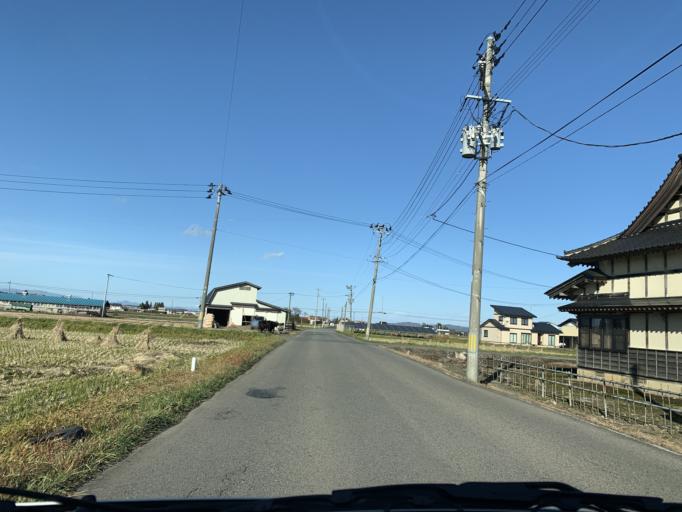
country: JP
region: Iwate
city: Mizusawa
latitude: 39.1536
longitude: 141.0970
